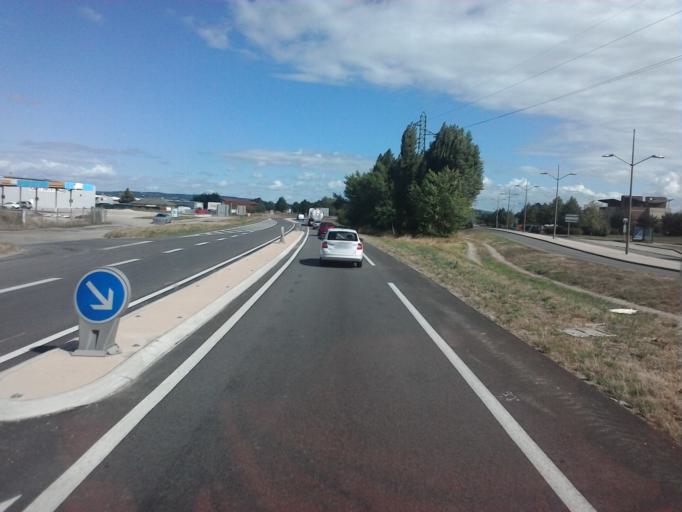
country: FR
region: Rhone-Alpes
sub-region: Departement de l'Ain
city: Amberieu-en-Bugey
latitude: 45.9794
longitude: 5.3488
